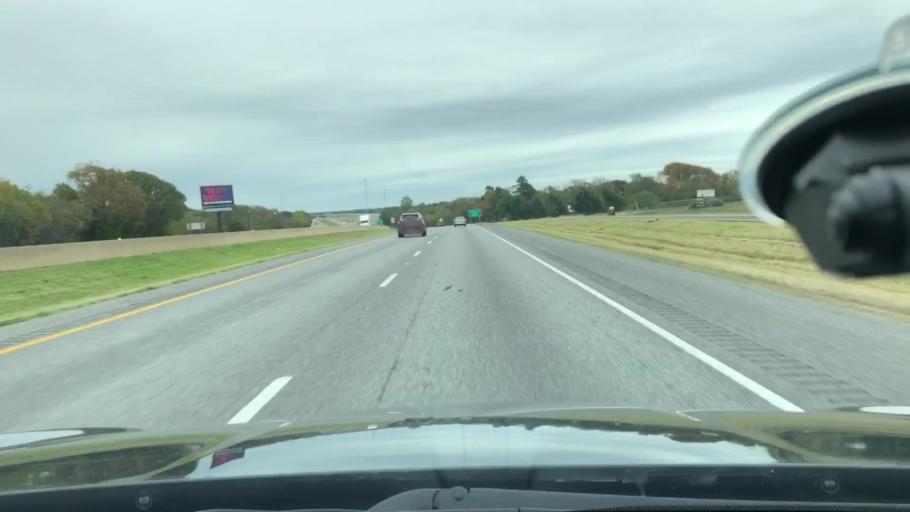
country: US
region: Texas
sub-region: Hunt County
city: Greenville
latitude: 33.1306
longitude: -96.0063
